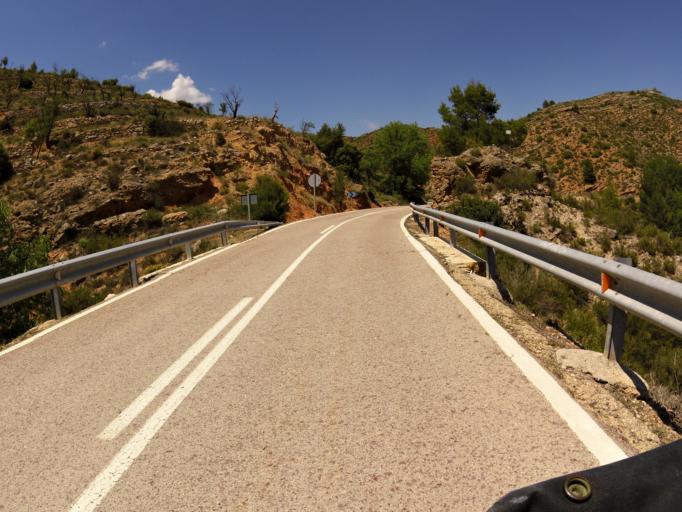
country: ES
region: Valencia
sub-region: Provincia de Valencia
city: Casas Bajas
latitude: 40.0119
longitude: -1.2722
